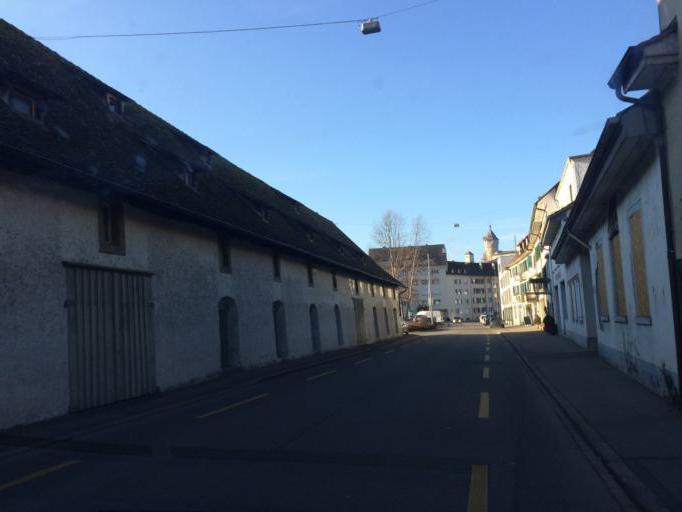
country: CH
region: Zurich
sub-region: Bezirk Andelfingen
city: Feuerthalen
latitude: 47.6947
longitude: 8.6461
